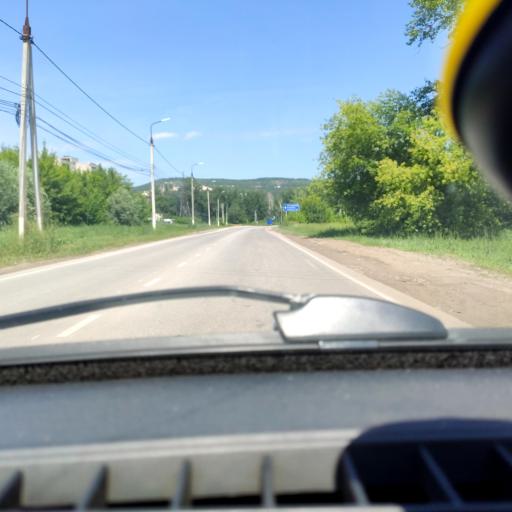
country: RU
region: Samara
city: Zhigulevsk
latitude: 53.3951
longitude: 49.5096
